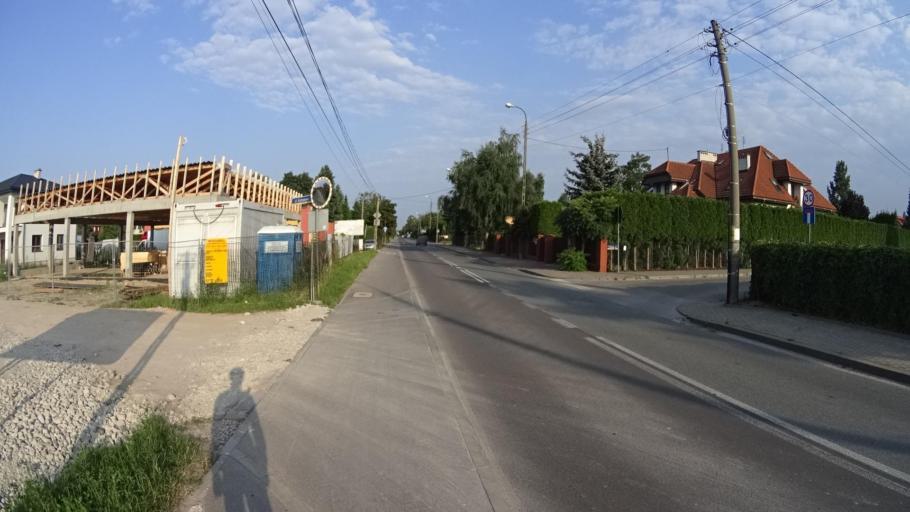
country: PL
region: Masovian Voivodeship
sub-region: Powiat pruszkowski
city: Rybie
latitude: 52.1485
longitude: 20.9412
